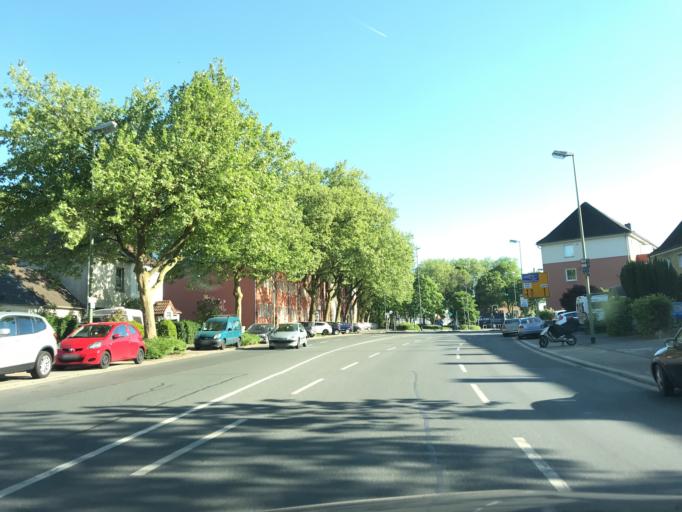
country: DE
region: North Rhine-Westphalia
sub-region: Regierungsbezirk Dusseldorf
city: Essen
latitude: 51.4607
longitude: 7.0482
